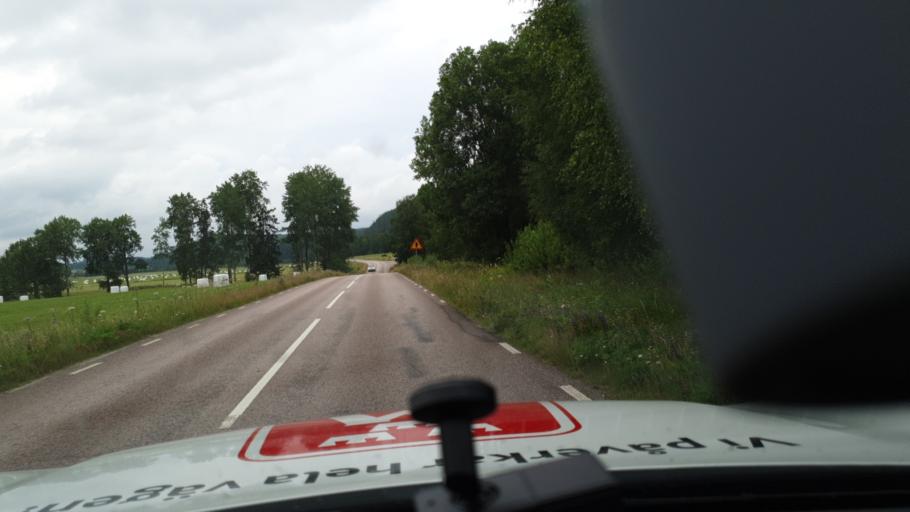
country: SE
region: Vaermland
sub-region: Sunne Kommun
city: Sunne
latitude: 59.8061
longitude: 13.2280
